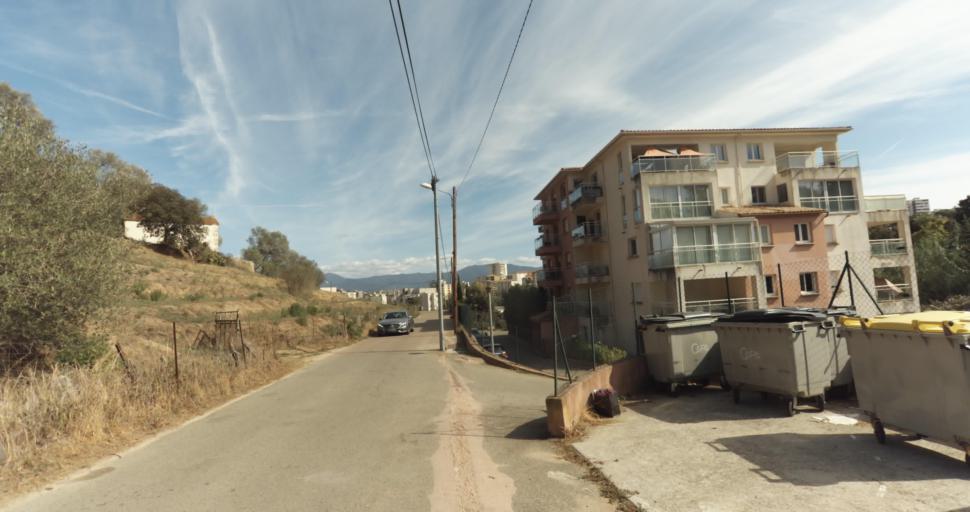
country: FR
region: Corsica
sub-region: Departement de la Corse-du-Sud
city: Ajaccio
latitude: 41.9377
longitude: 8.7310
